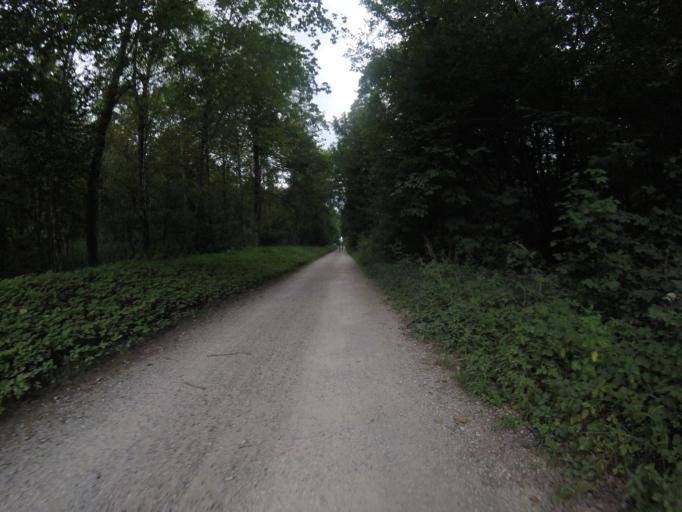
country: CH
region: Bern
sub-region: Bern-Mittelland District
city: Rubigen
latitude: 46.8772
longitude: 7.5361
